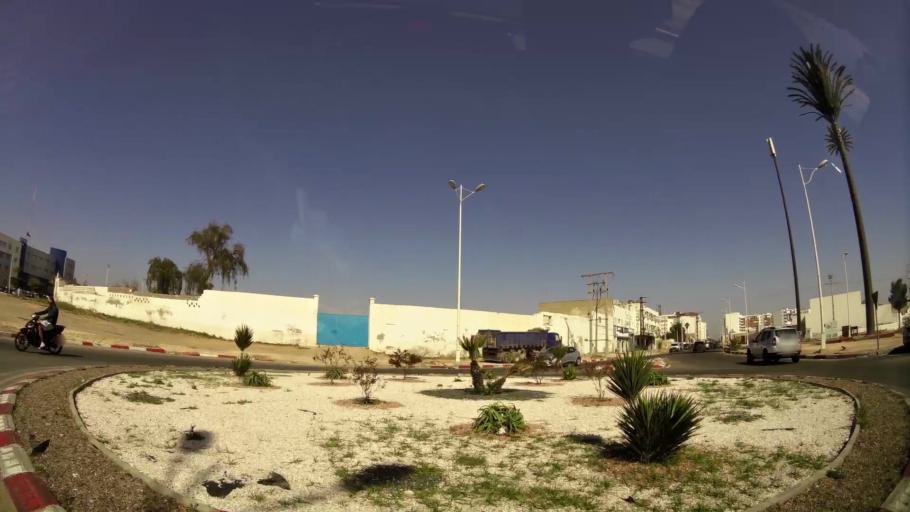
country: MA
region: Souss-Massa-Draa
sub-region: Agadir-Ida-ou-Tnan
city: Agadir
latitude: 30.4209
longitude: -9.5820
